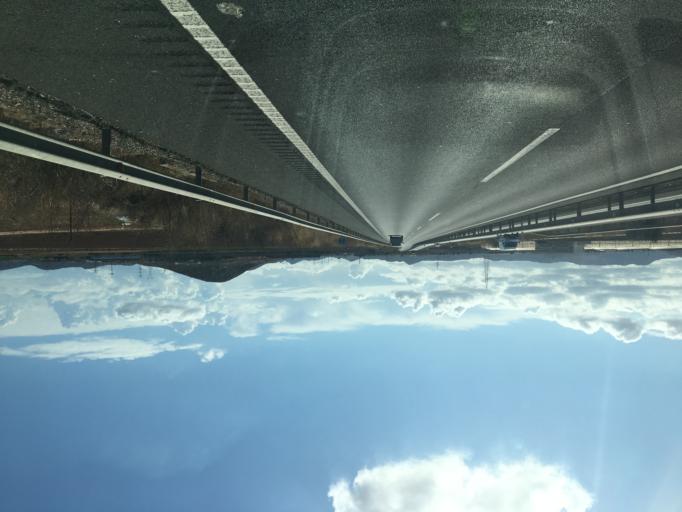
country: ES
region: Murcia
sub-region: Murcia
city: Cartagena
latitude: 37.6441
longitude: -0.9674
